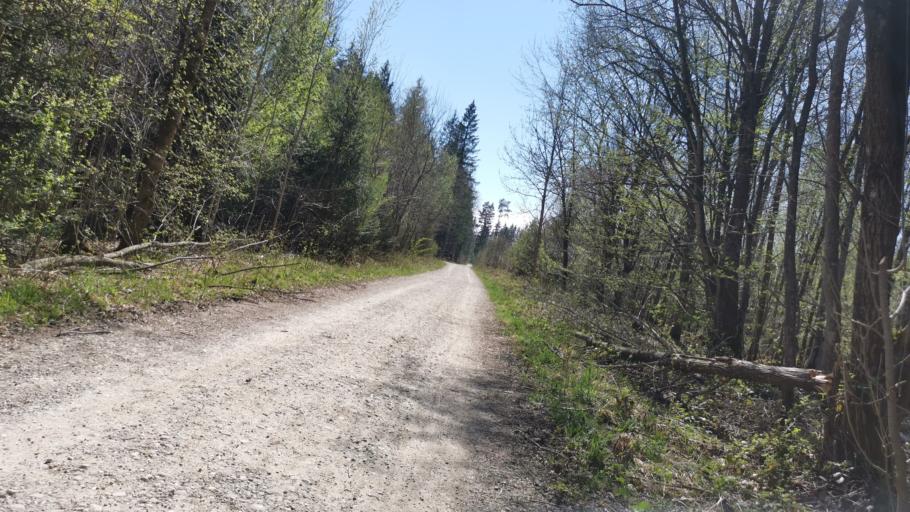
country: DE
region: Bavaria
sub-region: Upper Bavaria
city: Planegg
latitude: 48.0805
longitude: 11.4229
